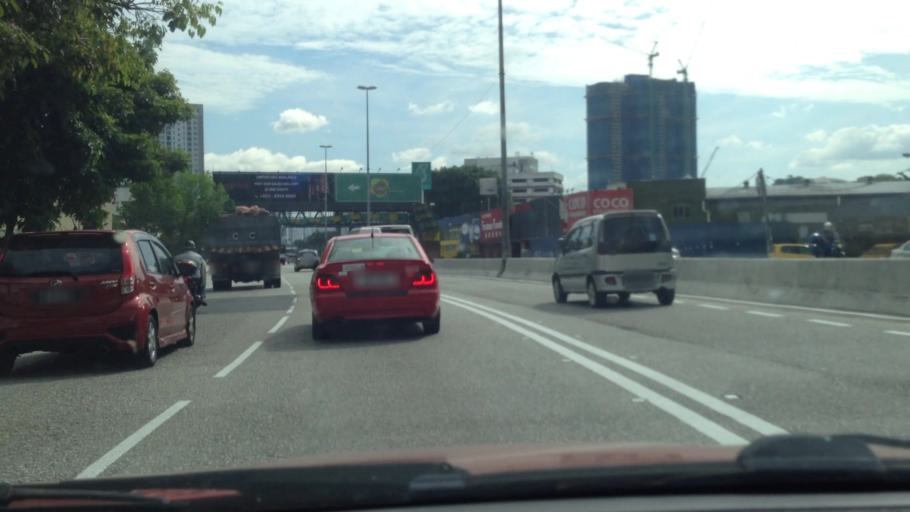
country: MY
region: Kuala Lumpur
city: Kuala Lumpur
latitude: 3.0870
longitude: 101.6738
